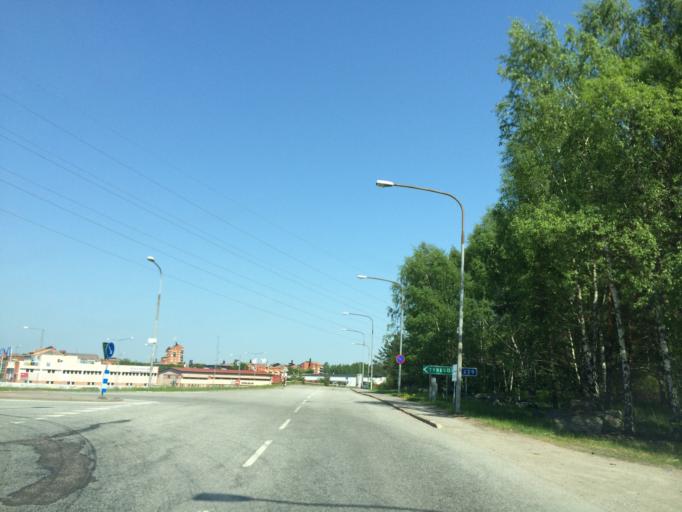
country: SE
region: Stockholm
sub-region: Nacka Kommun
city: Alta
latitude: 59.2620
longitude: 18.1255
